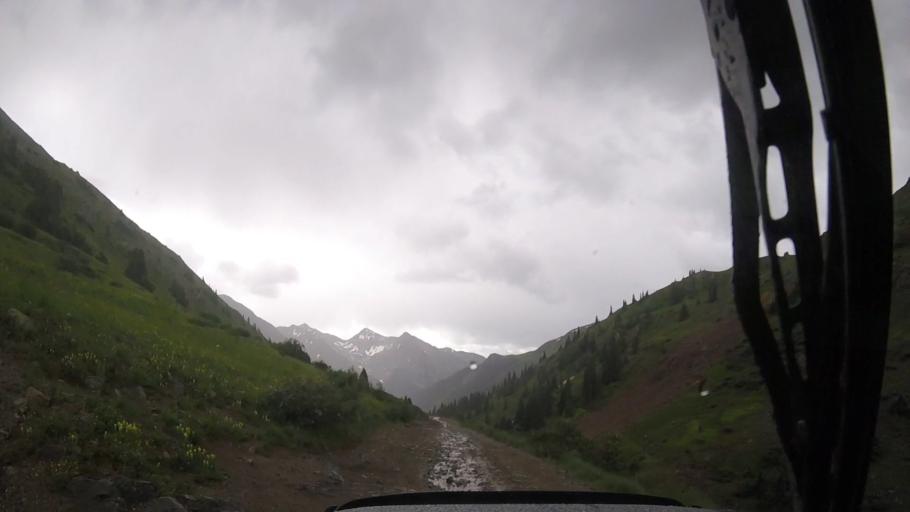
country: US
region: Colorado
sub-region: Ouray County
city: Ouray
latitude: 37.9395
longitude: -107.5733
